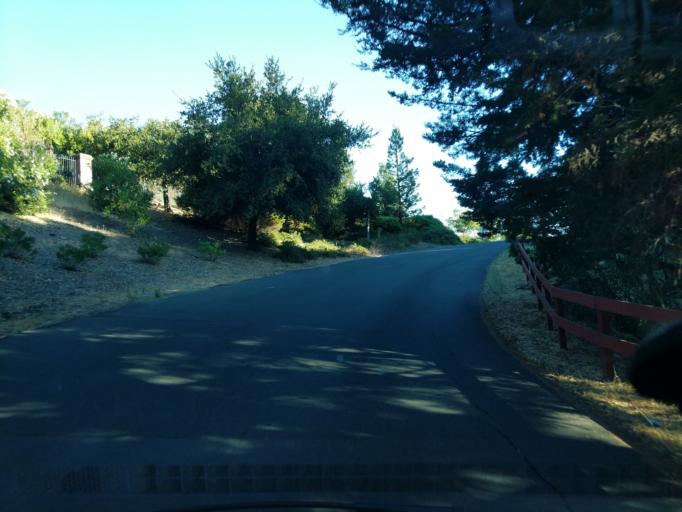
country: US
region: California
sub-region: Contra Costa County
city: Diablo
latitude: 37.8407
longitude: -121.9475
